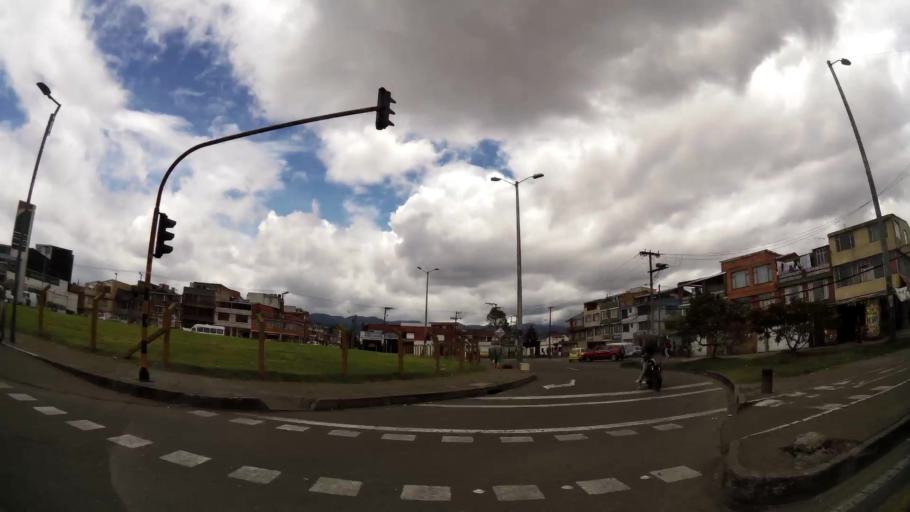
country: CO
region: Bogota D.C.
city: Bogota
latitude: 4.6881
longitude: -74.1105
